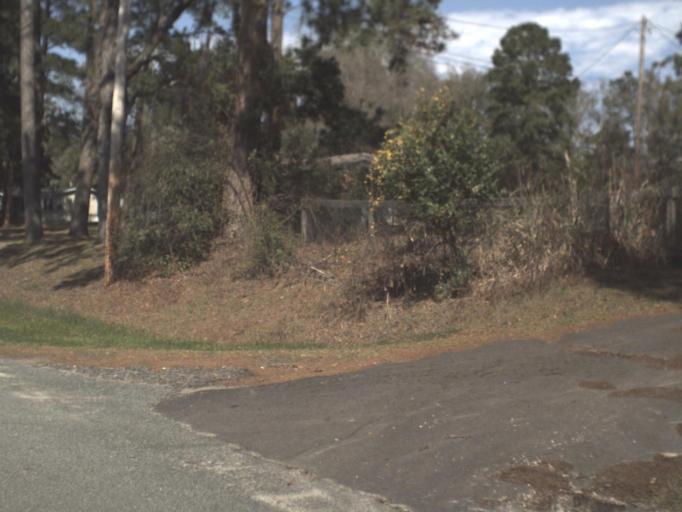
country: US
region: Florida
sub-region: Gadsden County
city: Quincy
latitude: 30.5972
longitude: -84.5372
